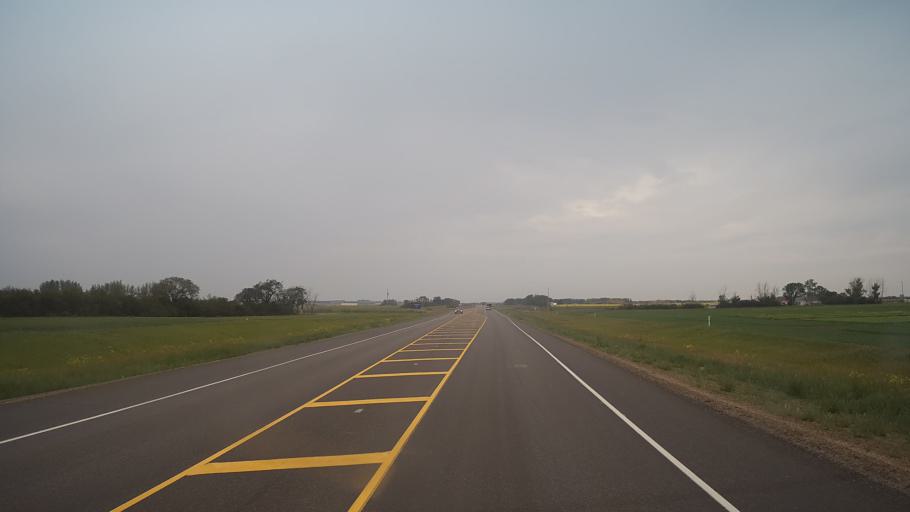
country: CA
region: Saskatchewan
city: Saskatoon
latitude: 52.1292
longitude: -106.8547
